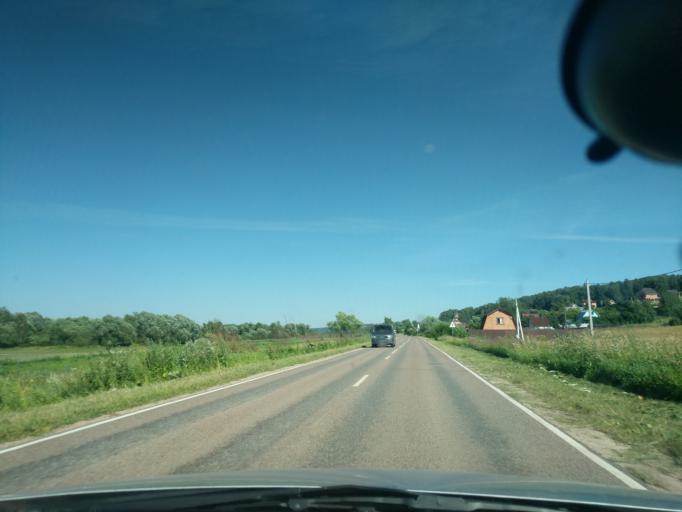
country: RU
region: Moskovskaya
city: Pushchino
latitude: 54.8440
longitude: 37.5341
